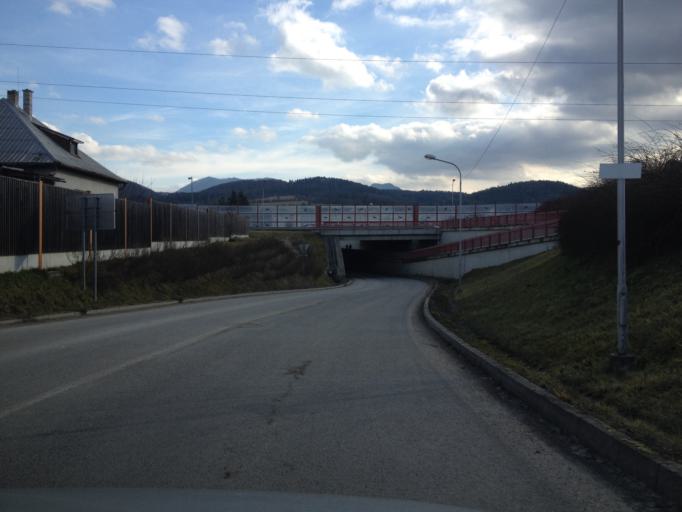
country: SK
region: Nitriansky
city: Puchov
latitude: 49.0577
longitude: 18.3288
